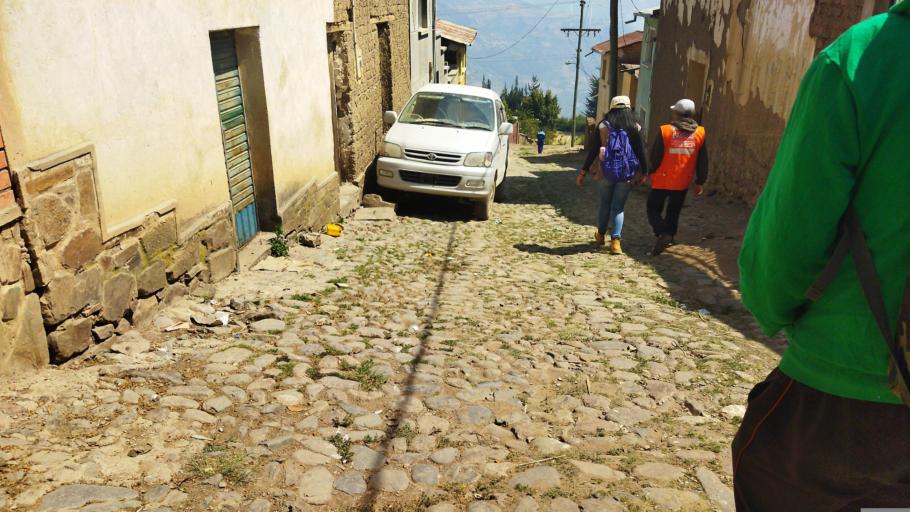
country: BO
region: La Paz
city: Quime
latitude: -16.9069
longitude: -67.1373
